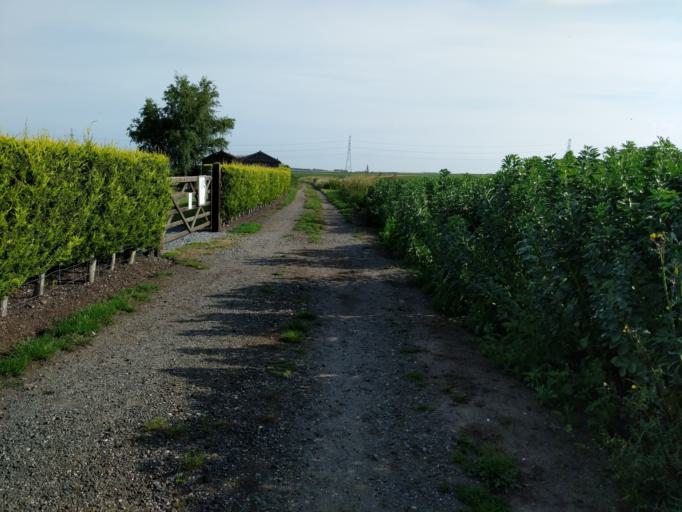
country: GB
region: England
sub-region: Kent
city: Faversham
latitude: 51.3317
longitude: 0.9147
